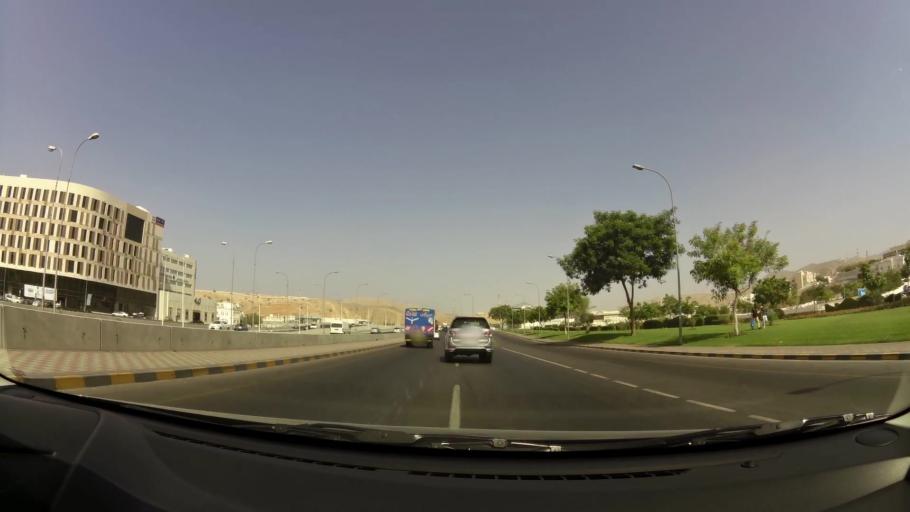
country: OM
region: Muhafazat Masqat
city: Muscat
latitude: 23.6105
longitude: 58.4949
